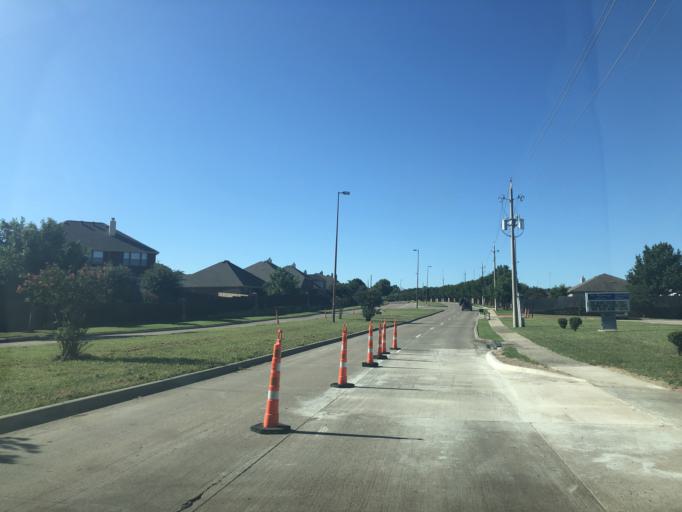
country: US
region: Texas
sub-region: Dallas County
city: Duncanville
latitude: 32.6585
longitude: -96.9711
